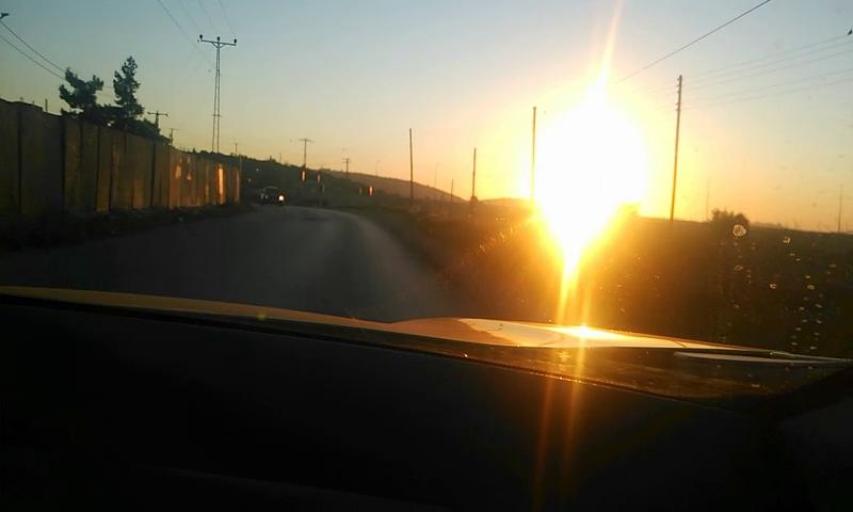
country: PS
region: West Bank
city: `Ayn Yabrud
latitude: 31.9597
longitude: 35.2592
